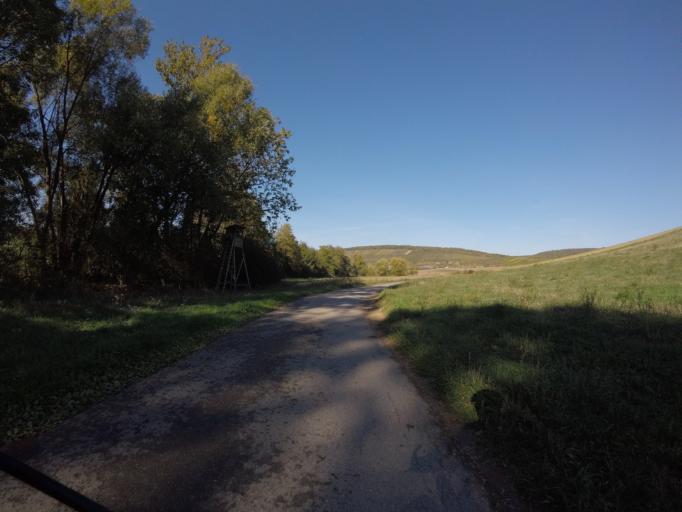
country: DE
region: Baden-Wuerttemberg
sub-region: Karlsruhe Region
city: Illingen
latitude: 48.9895
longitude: 8.9594
